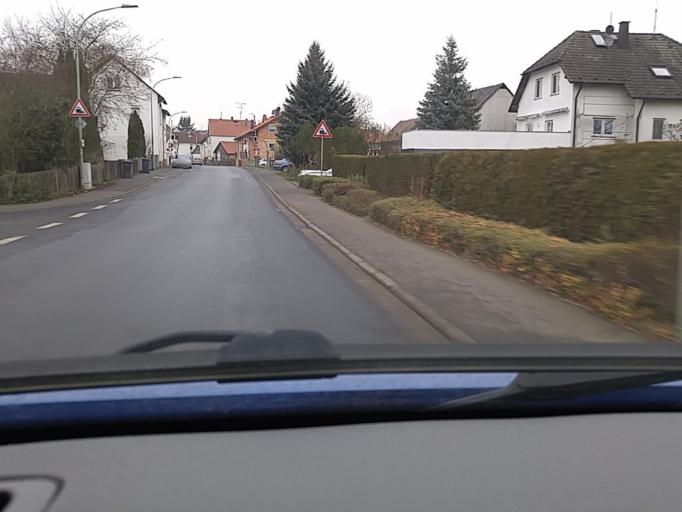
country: DE
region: Hesse
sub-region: Regierungsbezirk Darmstadt
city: Echzell
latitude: 50.3913
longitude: 8.8933
